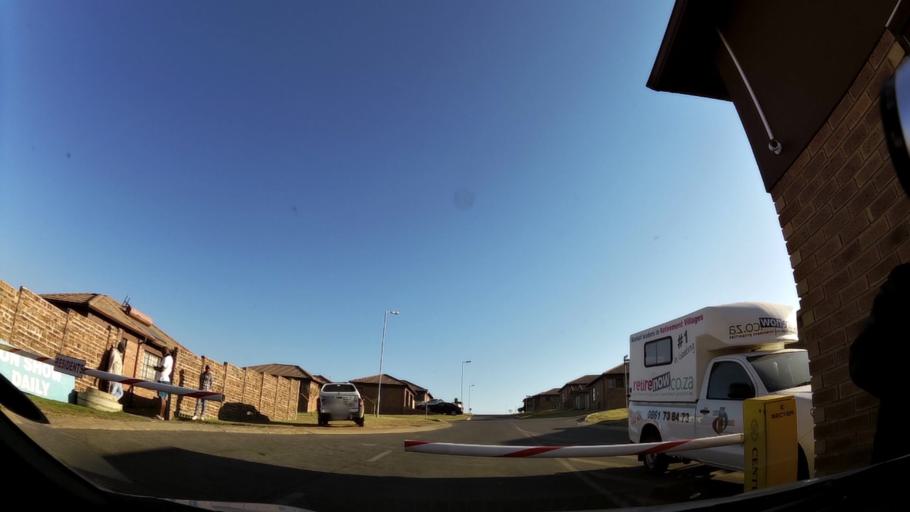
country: ZA
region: Gauteng
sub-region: City of Johannesburg Metropolitan Municipality
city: Midrand
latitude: -25.9092
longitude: 28.1050
